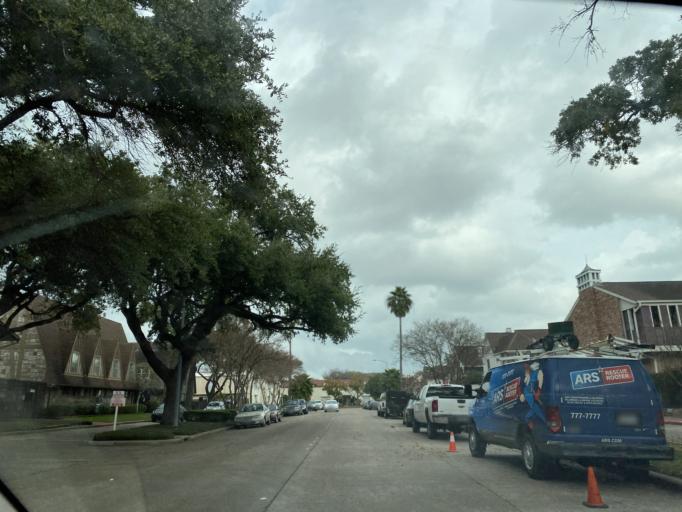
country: US
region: Texas
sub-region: Harris County
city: Piney Point Village
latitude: 29.7397
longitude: -95.4984
